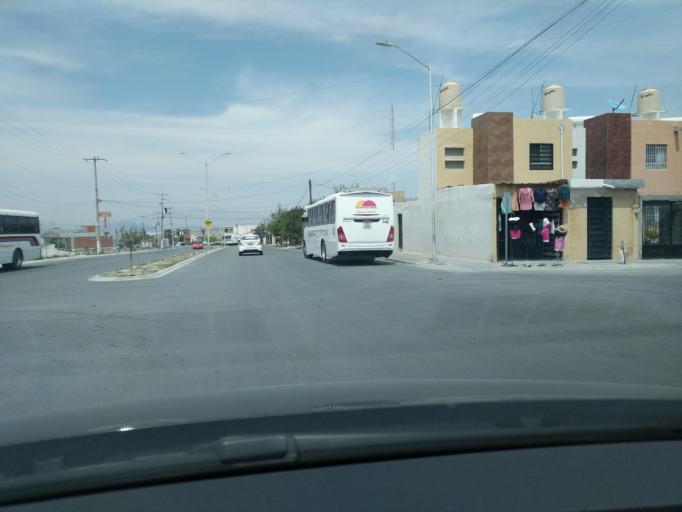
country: MX
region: Coahuila
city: Saltillo
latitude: 25.3477
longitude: -101.0091
